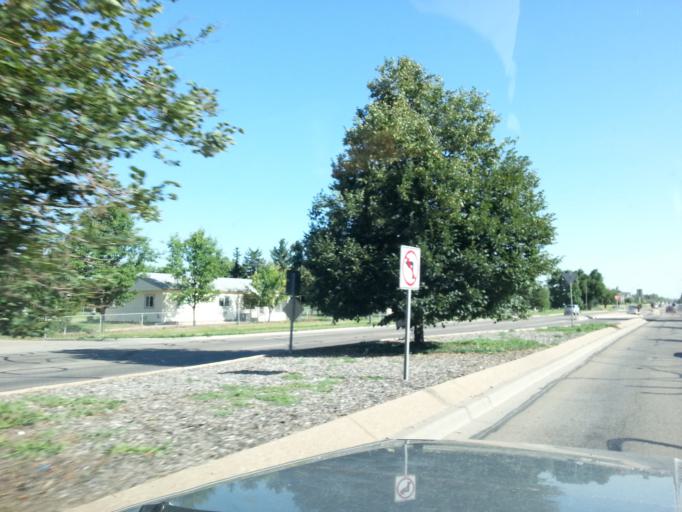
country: US
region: Colorado
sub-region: Larimer County
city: Fort Collins
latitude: 40.5242
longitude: -105.0393
